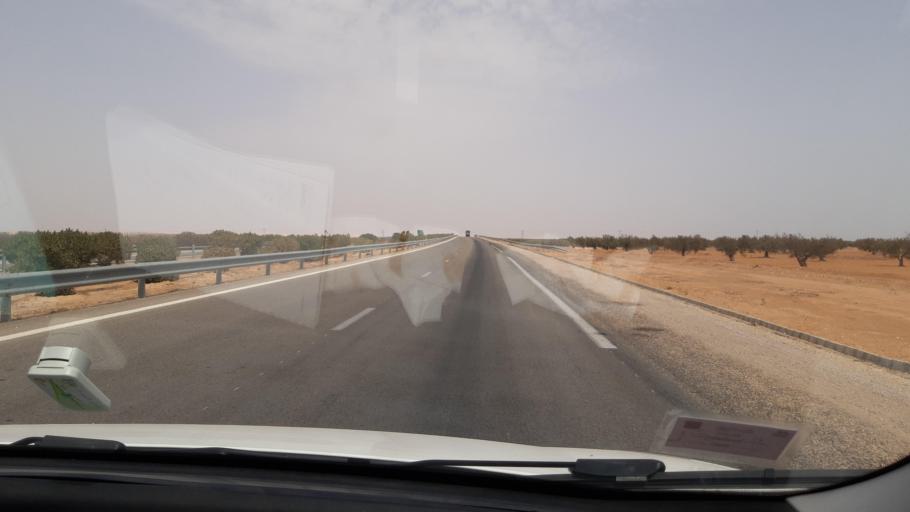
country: TN
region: Safaqis
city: Bi'r `Ali Bin Khalifah
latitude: 34.5462
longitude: 10.3142
